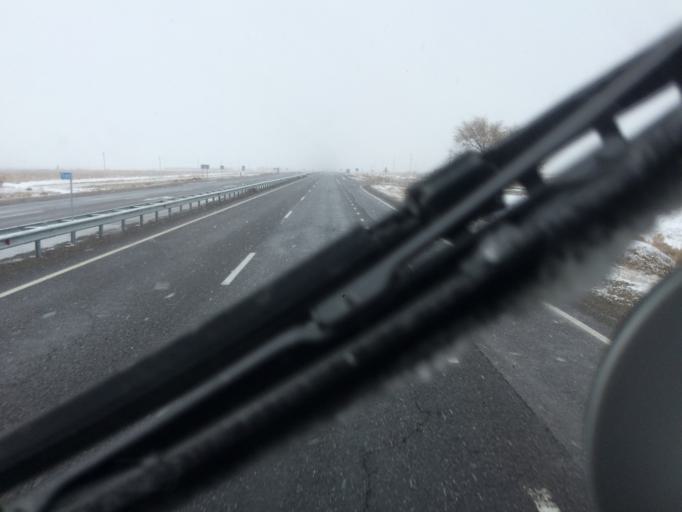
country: KZ
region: Ongtustik Qazaqstan
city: Turkestan
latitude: 43.4562
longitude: 67.9359
